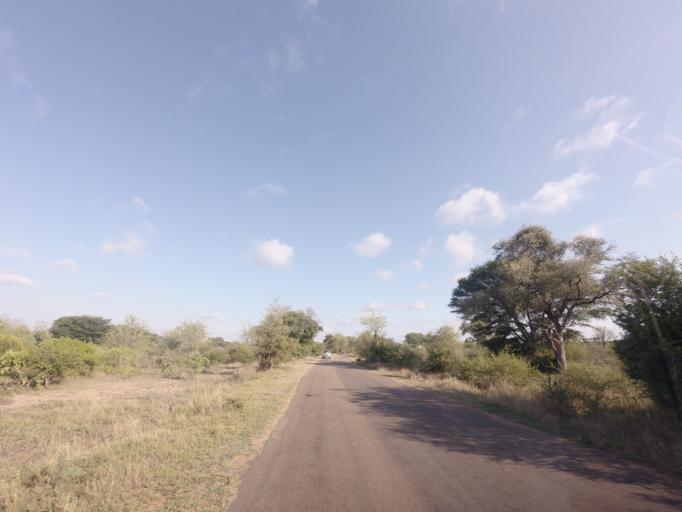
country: ZA
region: Mpumalanga
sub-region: Ehlanzeni District
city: Komatipoort
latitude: -25.2639
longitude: 31.8465
